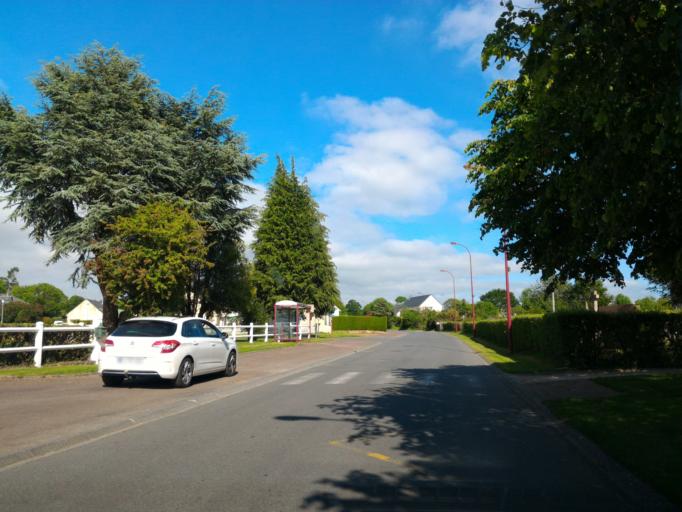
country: FR
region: Lower Normandy
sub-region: Departement de la Manche
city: Percy
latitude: 48.8747
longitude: -1.1822
